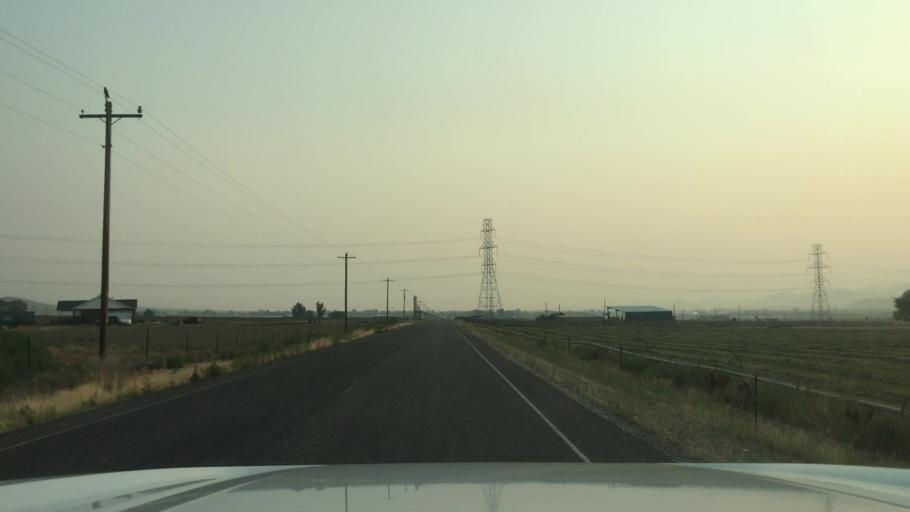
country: US
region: Utah
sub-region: Sevier County
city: Aurora
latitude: 38.8954
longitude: -111.9510
